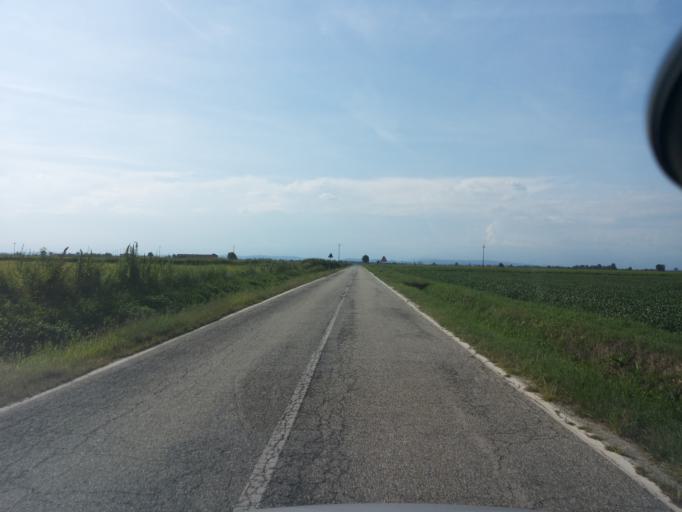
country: IT
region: Piedmont
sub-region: Provincia di Vercelli
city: Salasco
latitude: 45.3000
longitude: 8.2668
